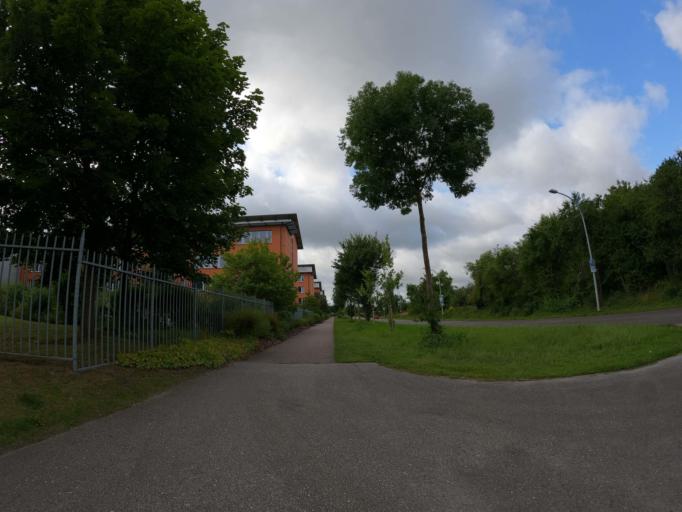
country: DE
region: Mecklenburg-Vorpommern
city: Kramerhof
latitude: 54.3394
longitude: 13.0666
